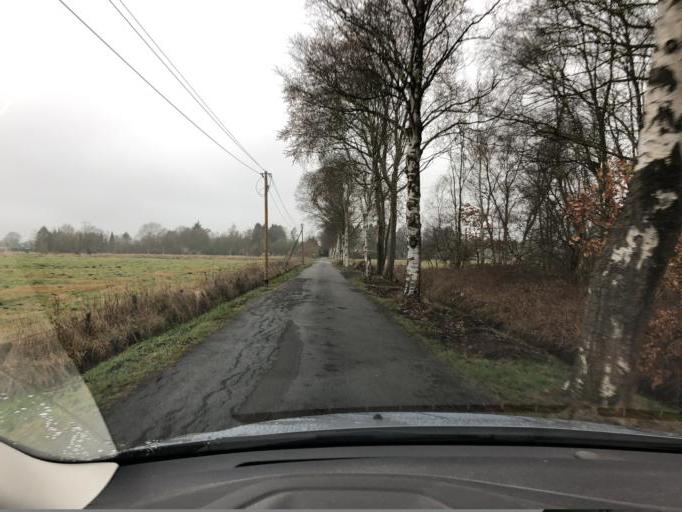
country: DE
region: Lower Saxony
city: Bad Zwischenahn
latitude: 53.1696
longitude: 8.0209
